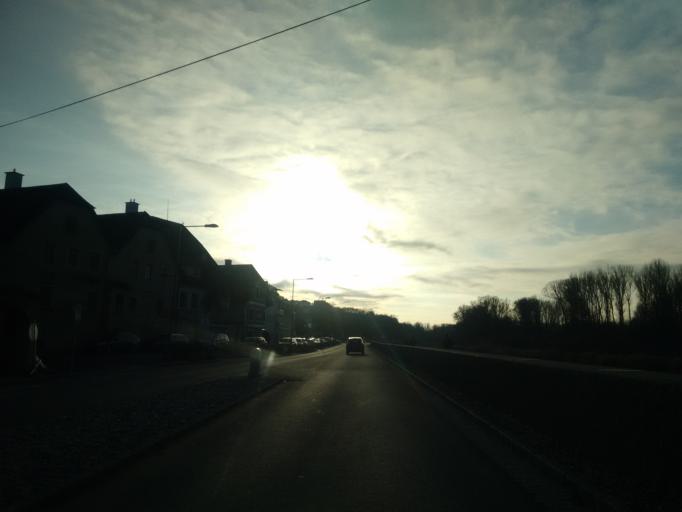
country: AT
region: Lower Austria
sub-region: Politischer Bezirk Melk
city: Melk
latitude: 48.2277
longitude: 15.3282
